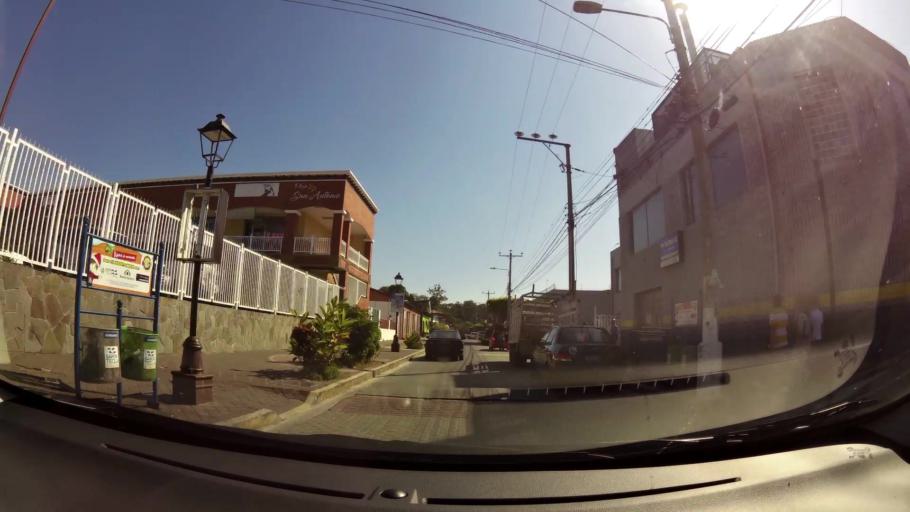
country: SV
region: La Libertad
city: Santa Tecla
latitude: 13.6753
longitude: -89.2857
